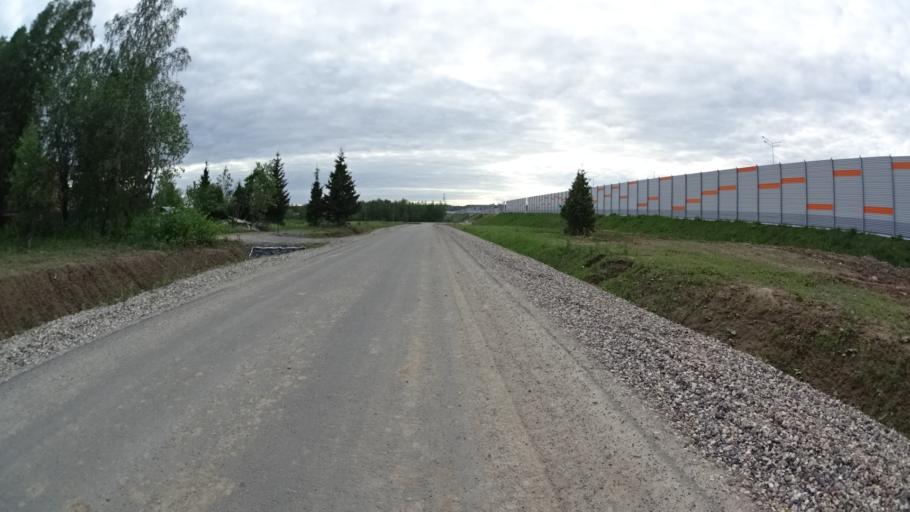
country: RU
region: Moskovskaya
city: Zelenogradskiy
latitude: 56.1255
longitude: 37.9046
